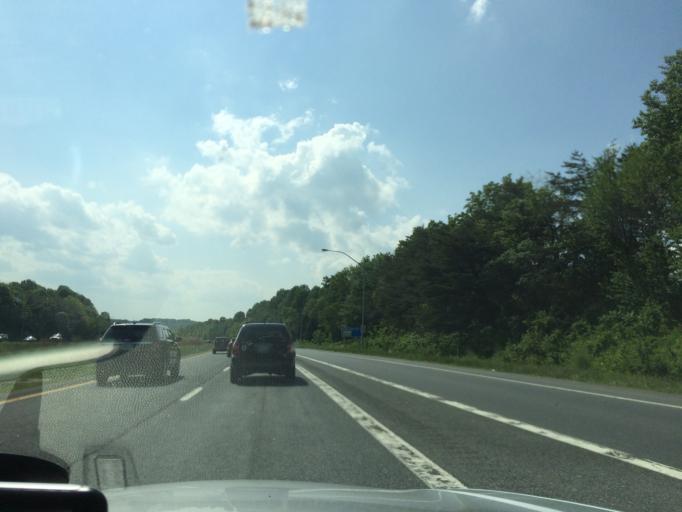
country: US
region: Maryland
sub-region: Howard County
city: Riverside
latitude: 39.1832
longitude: -76.8792
